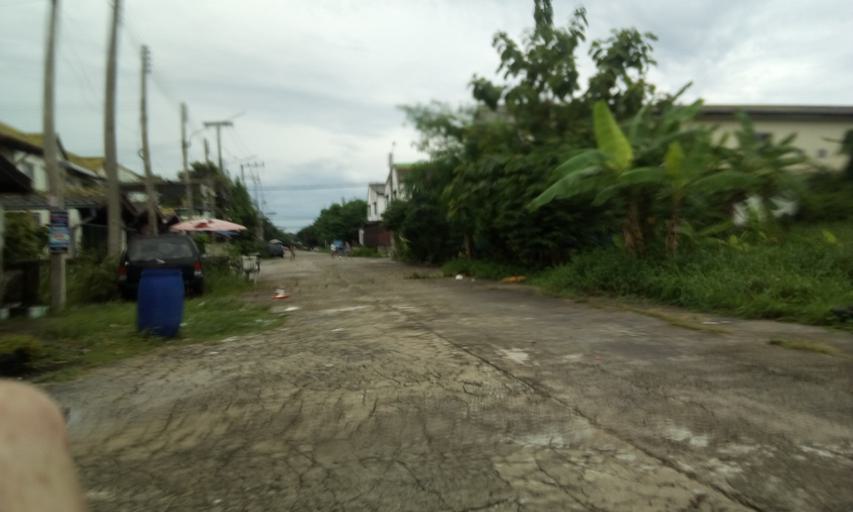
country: TH
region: Pathum Thani
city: Ban Rangsit
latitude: 14.0395
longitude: 100.8297
